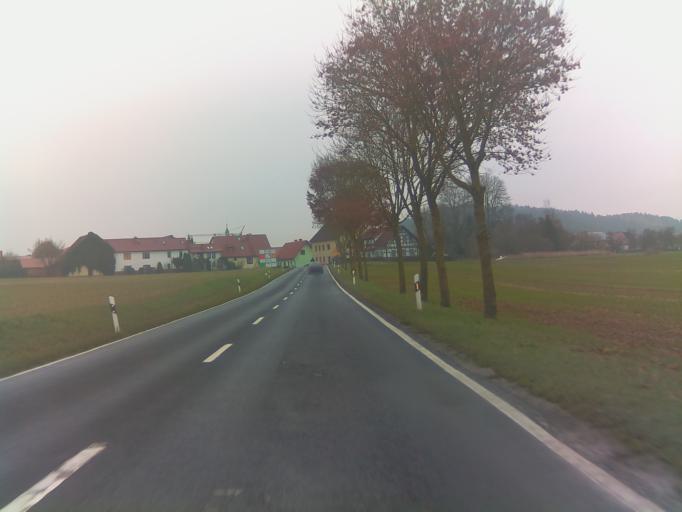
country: DE
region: Thuringia
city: Juchsen
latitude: 50.4615
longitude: 10.5416
